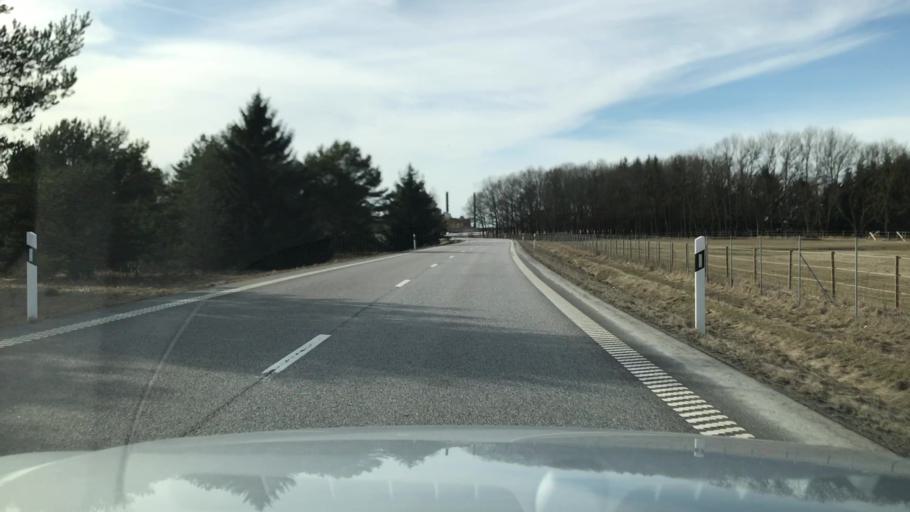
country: SE
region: OEstergoetland
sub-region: Linkopings Kommun
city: Ekangen
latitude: 58.4340
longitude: 15.6782
